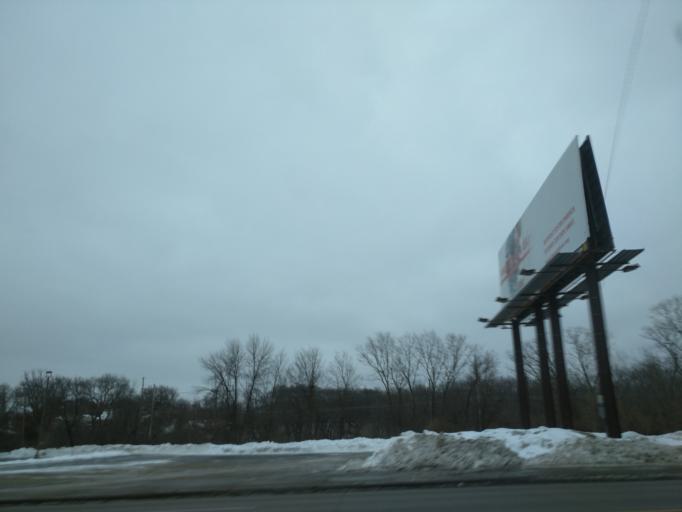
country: US
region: Wisconsin
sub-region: La Crosse County
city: North La Crosse
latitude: 43.8310
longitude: -91.2396
